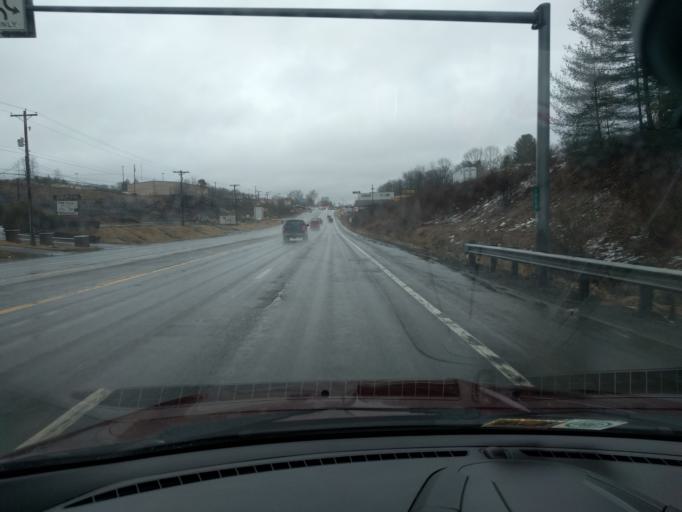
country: US
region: West Virginia
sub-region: Raleigh County
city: MacArthur
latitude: 37.7495
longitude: -81.2214
